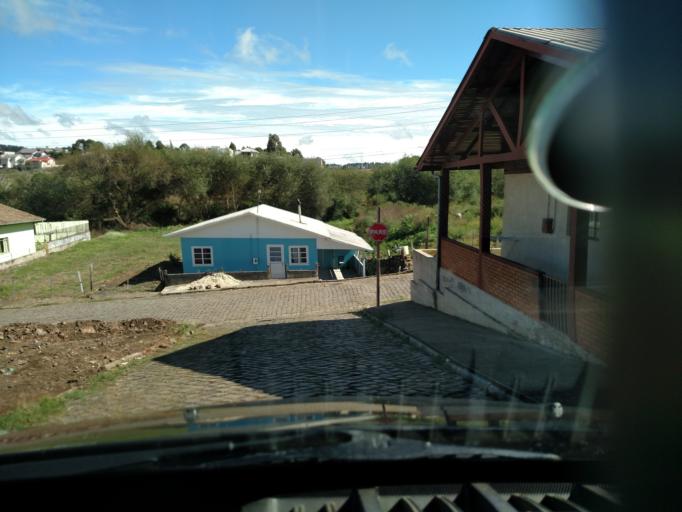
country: BR
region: Santa Catarina
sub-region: Sao Joaquim
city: Sao Joaquim
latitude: -28.2918
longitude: -49.9288
